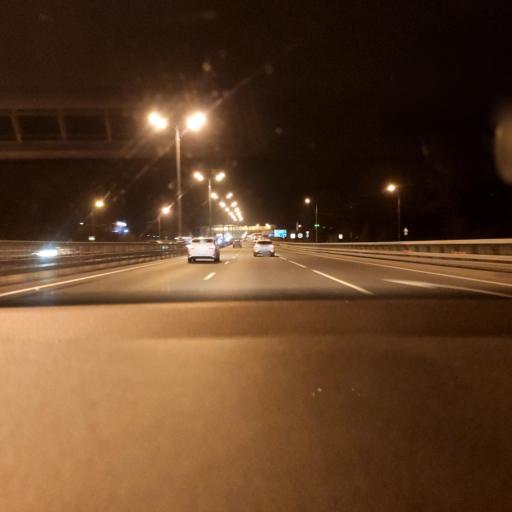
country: RU
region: Moskovskaya
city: Selyatino
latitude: 55.5155
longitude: 36.9938
